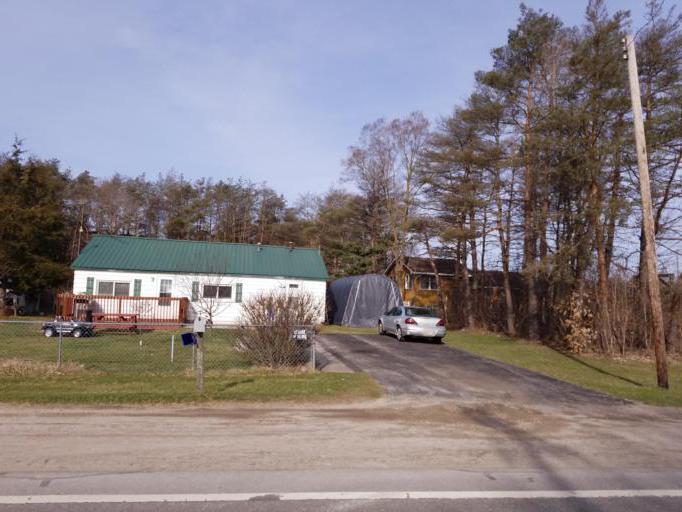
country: US
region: Michigan
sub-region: Montcalm County
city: Howard City
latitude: 43.4970
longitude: -85.4447
